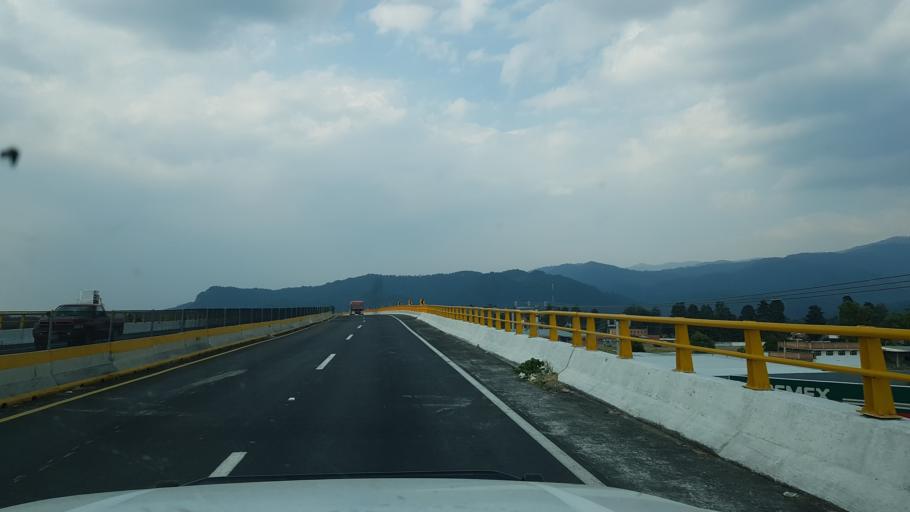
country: MX
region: Mexico
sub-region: Ayapango
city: La Colonia
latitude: 19.1367
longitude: -98.7769
